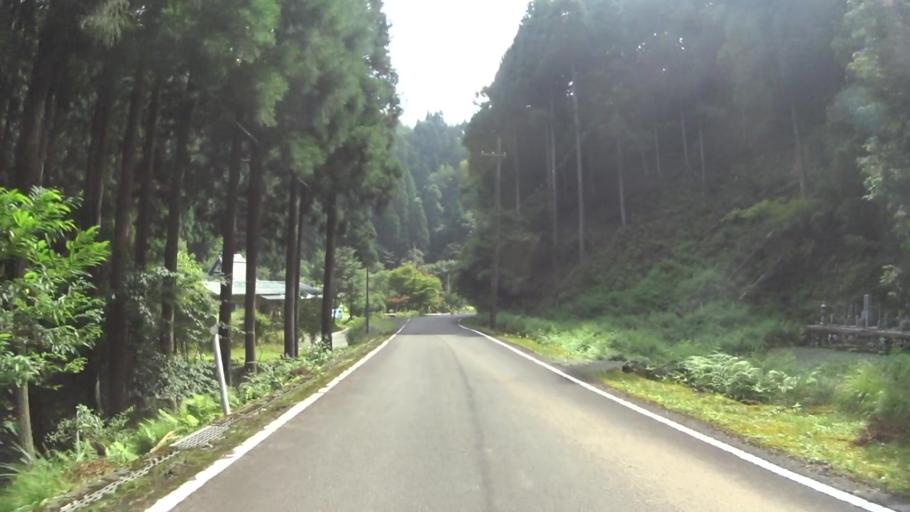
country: JP
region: Fukui
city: Obama
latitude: 35.3440
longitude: 135.6500
